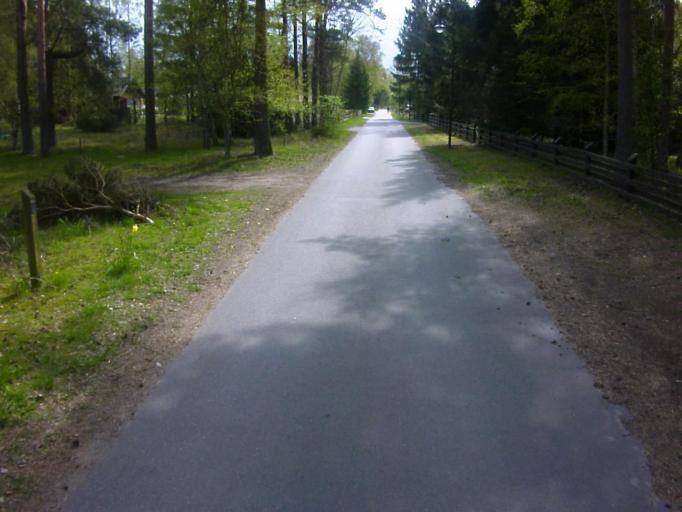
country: SE
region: Skane
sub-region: Kavlinge Kommun
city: Loddekopinge
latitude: 55.7623
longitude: 12.9878
